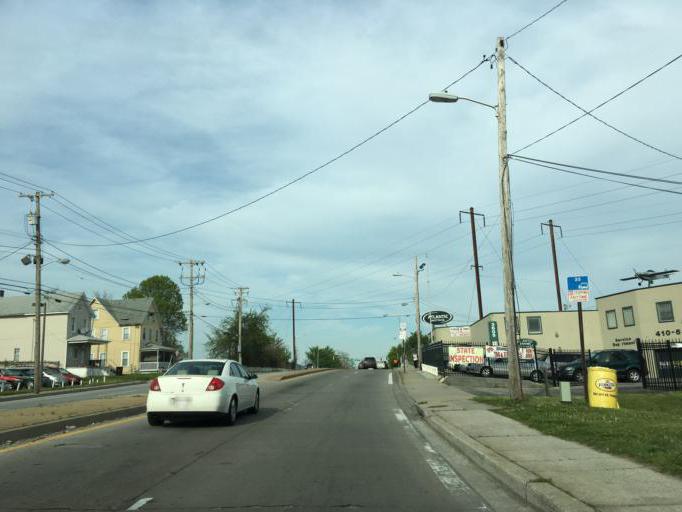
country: US
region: Maryland
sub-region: Baltimore County
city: Charlestown
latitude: 39.2707
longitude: -76.6807
